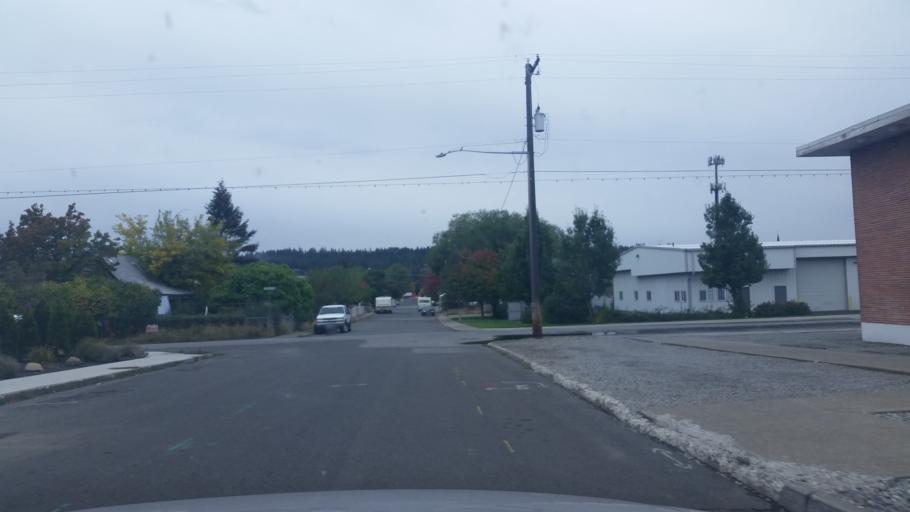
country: US
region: Washington
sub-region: Spokane County
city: Spokane
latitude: 47.6596
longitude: -117.3798
